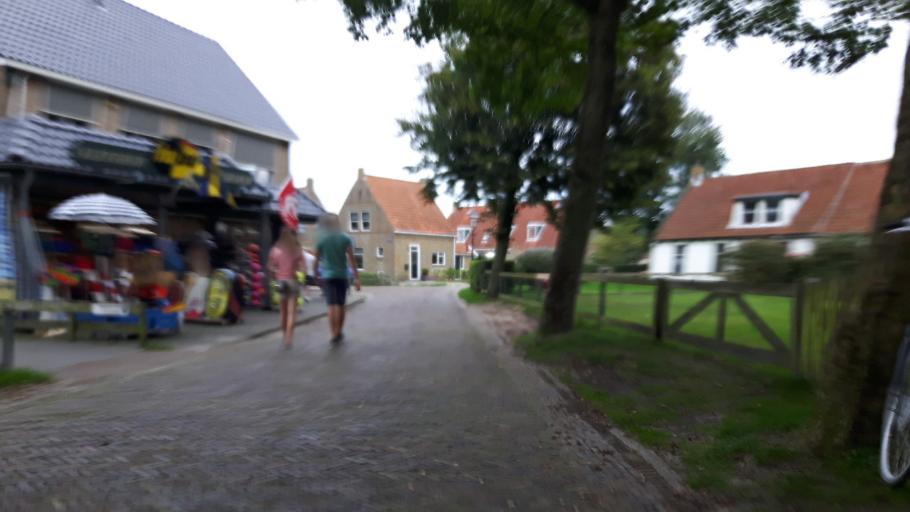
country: NL
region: Friesland
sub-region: Gemeente Ameland
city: Nes
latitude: 53.4463
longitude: 5.7717
